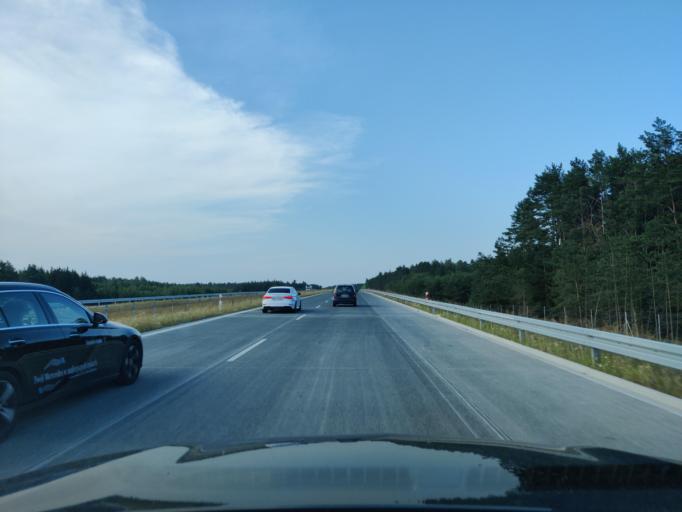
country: PL
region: Masovian Voivodeship
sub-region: Powiat mlawski
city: Strzegowo
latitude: 52.9049
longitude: 20.2738
